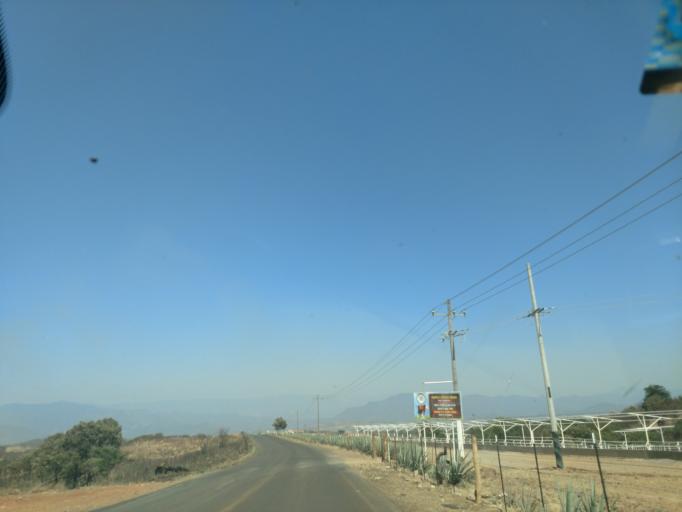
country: MX
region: Nayarit
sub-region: Tepic
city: La Corregidora
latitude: 21.4933
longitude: -104.6917
